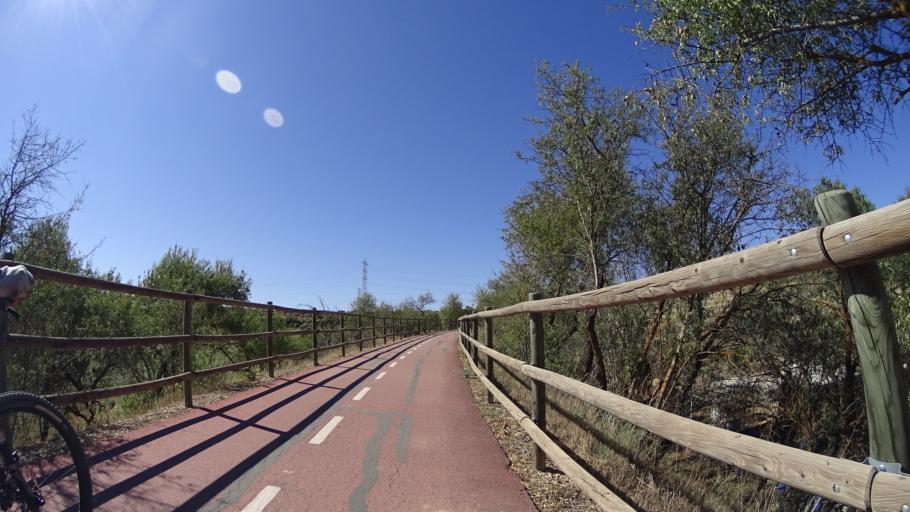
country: ES
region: Madrid
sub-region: Provincia de Madrid
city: Morata de Tajuna
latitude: 40.2606
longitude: -3.4685
